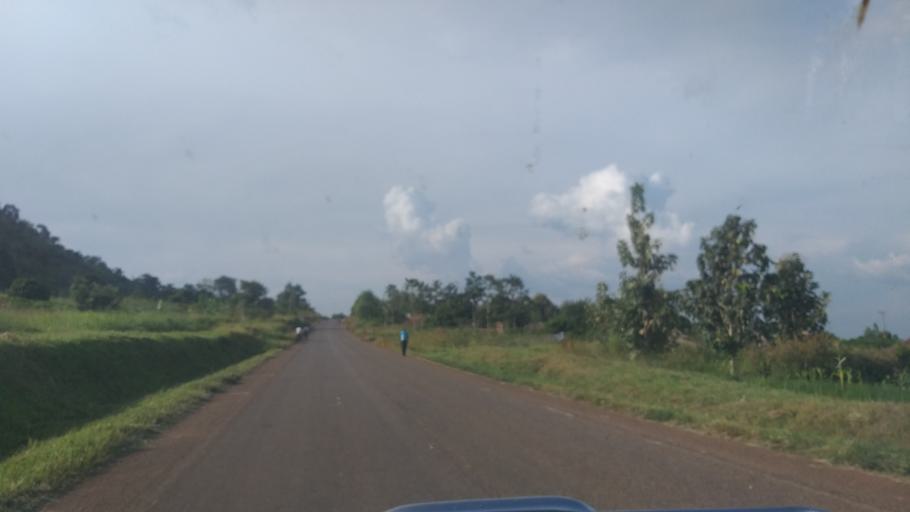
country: UG
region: Northern Region
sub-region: Arua District
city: Arua
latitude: 2.8345
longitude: 30.9936
